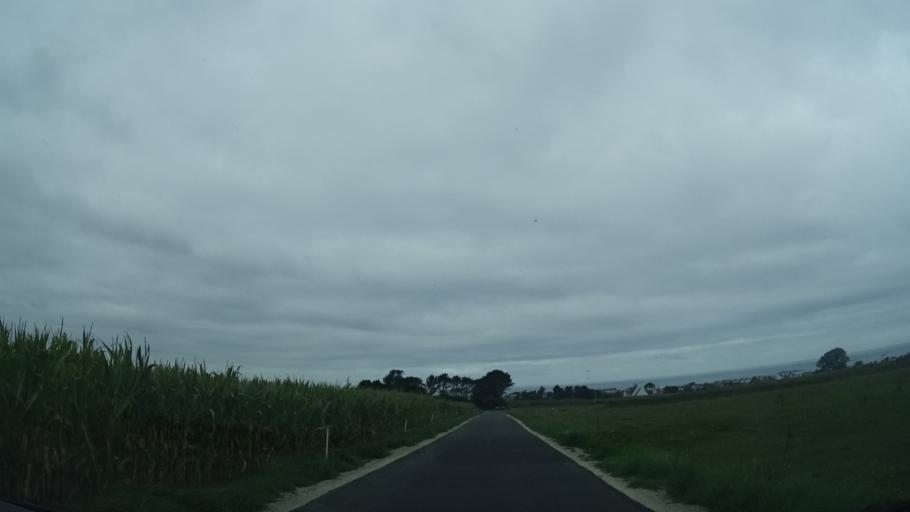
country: FR
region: Brittany
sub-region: Departement du Finistere
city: Lampaul-Plouarzel
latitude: 48.4587
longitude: -4.7501
